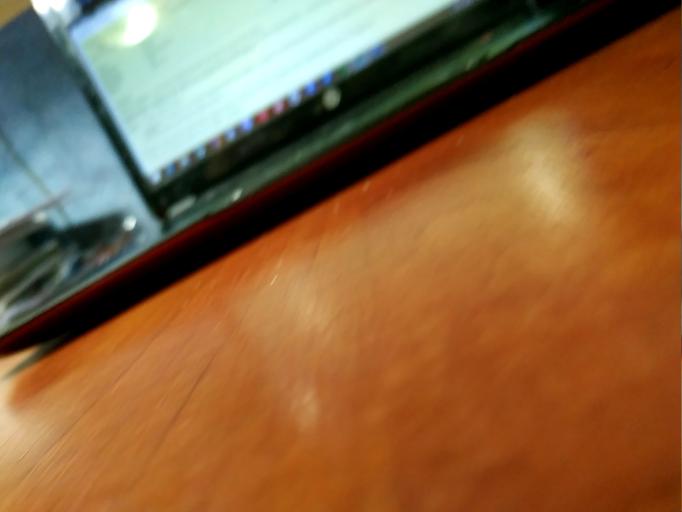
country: RU
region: Tverskaya
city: Sandovo
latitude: 58.4699
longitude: 36.3932
